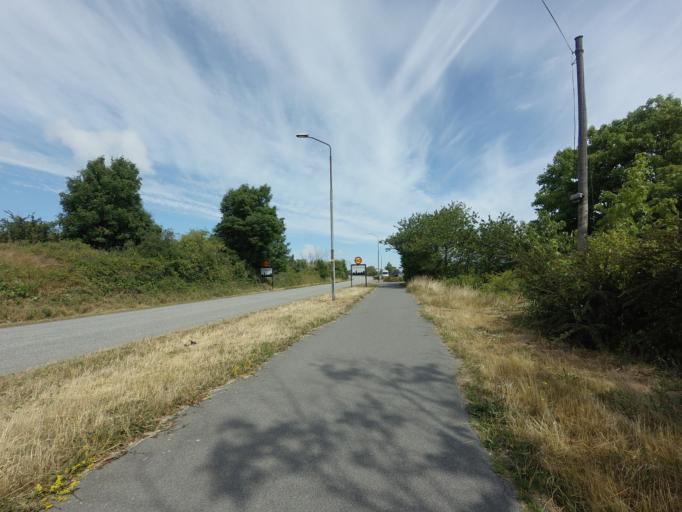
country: SE
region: Skane
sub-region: Simrishamns Kommun
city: Simrishamn
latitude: 55.5382
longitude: 14.3557
